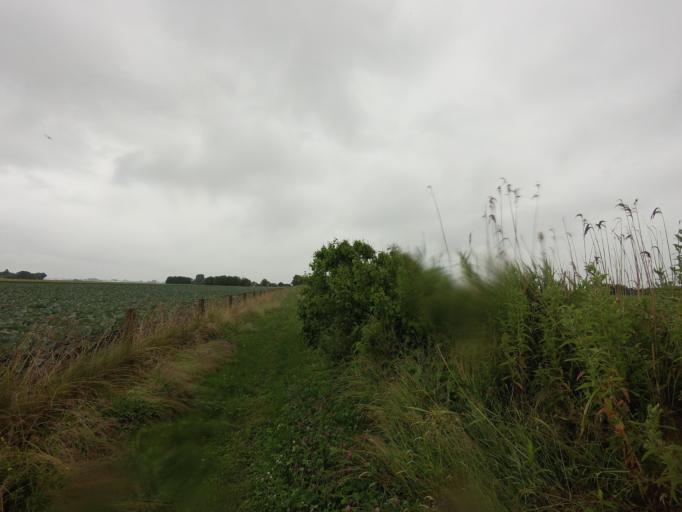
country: NL
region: North Holland
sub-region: Gemeente Schagen
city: Schagen
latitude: 52.7683
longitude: 4.8006
